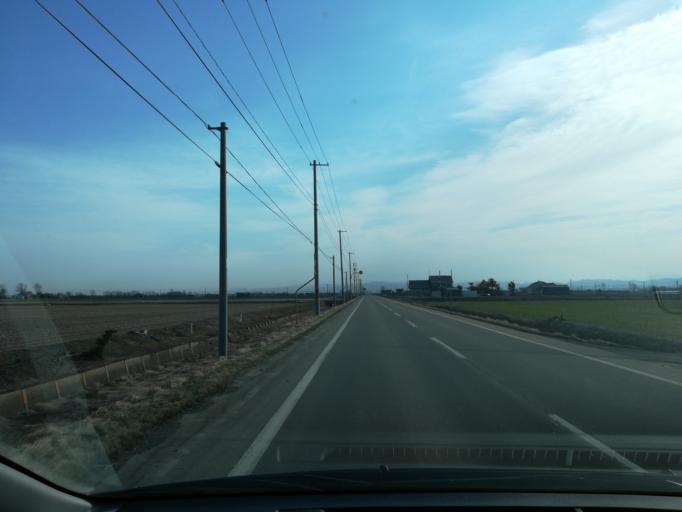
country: JP
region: Hokkaido
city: Iwamizawa
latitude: 43.1836
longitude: 141.6941
